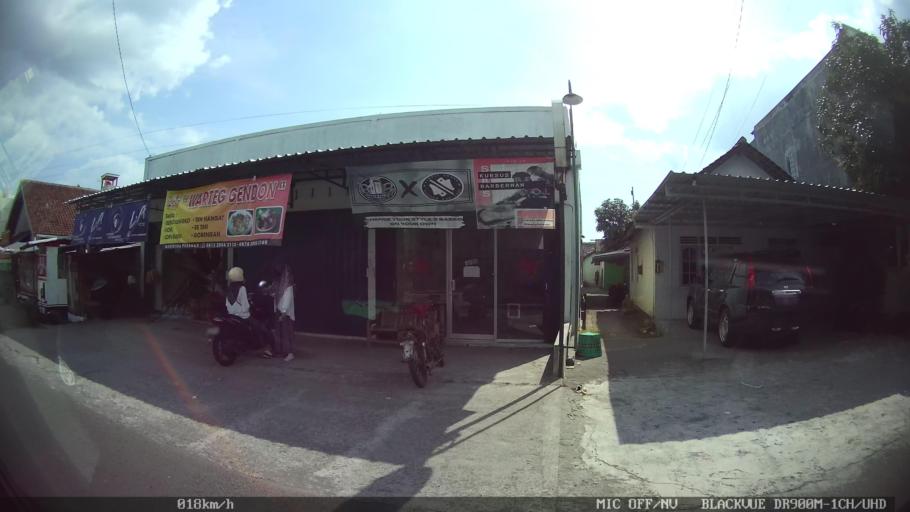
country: ID
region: Daerah Istimewa Yogyakarta
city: Kasihan
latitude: -7.8131
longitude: 110.3282
